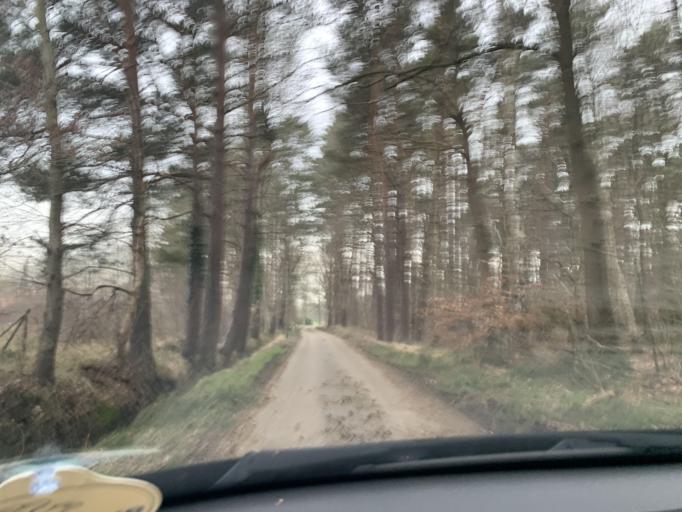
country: DE
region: Lower Saxony
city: Bad Zwischenahn
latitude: 53.2163
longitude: 7.9852
